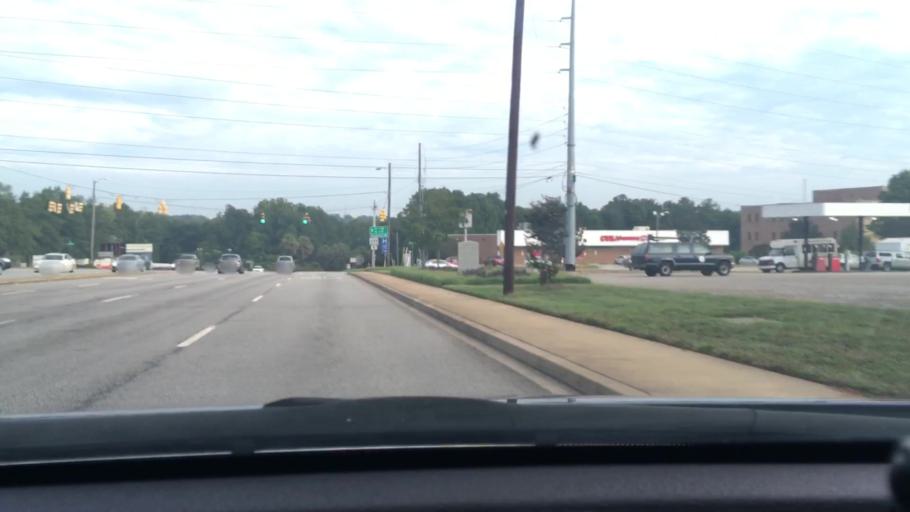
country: US
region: South Carolina
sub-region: Richland County
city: Columbia
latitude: 34.0233
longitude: -81.0377
